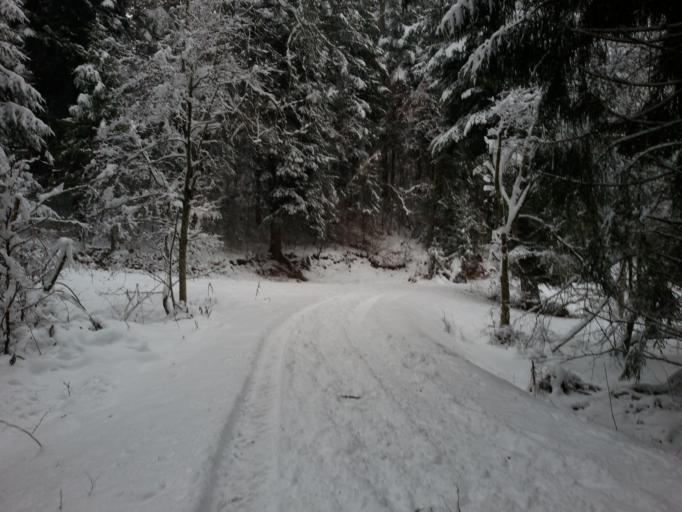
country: CH
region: Zurich
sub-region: Bezirk Hinwil
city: Rueti / Westlicher Dorfteil
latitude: 47.2535
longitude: 8.8304
